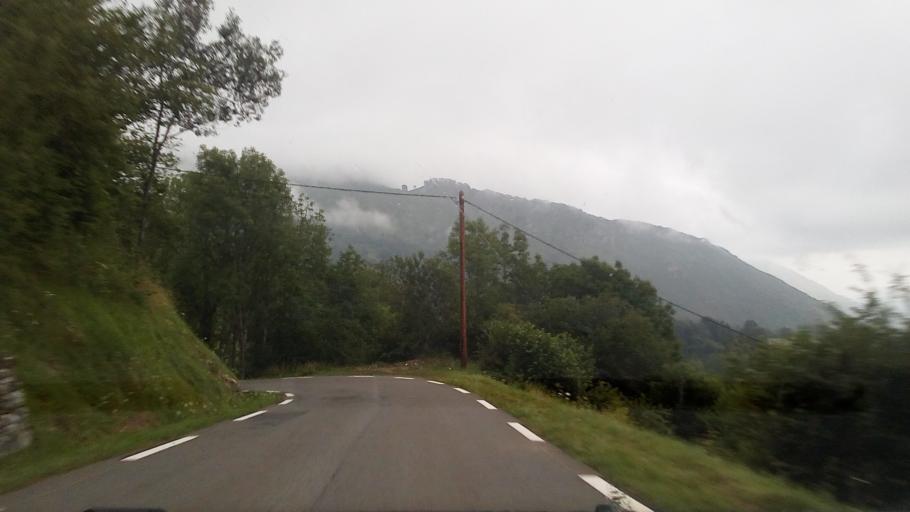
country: FR
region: Midi-Pyrenees
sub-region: Departement des Hautes-Pyrenees
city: Cauterets
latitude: 42.9633
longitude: -0.2310
